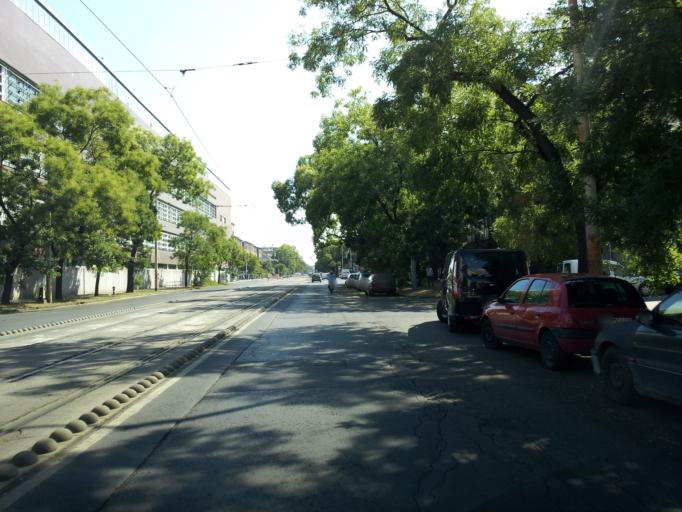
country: HU
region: Budapest
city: Budapest XI. keruelet
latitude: 47.4689
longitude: 19.0445
